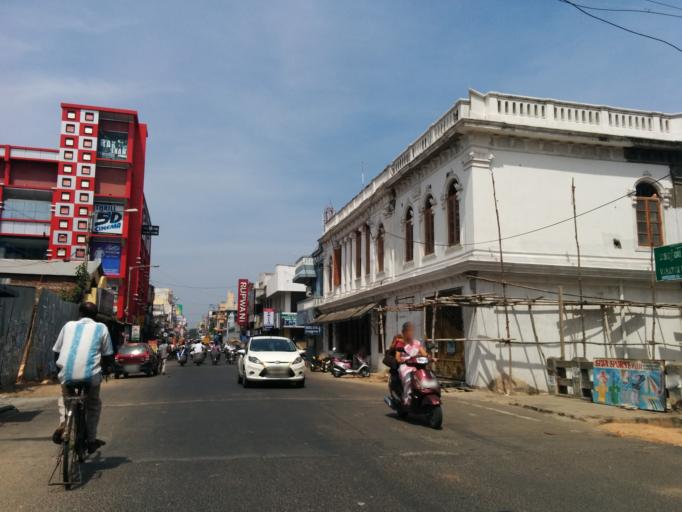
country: IN
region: Pondicherry
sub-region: Puducherry
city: Puducherry
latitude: 11.9320
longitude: 79.8285
